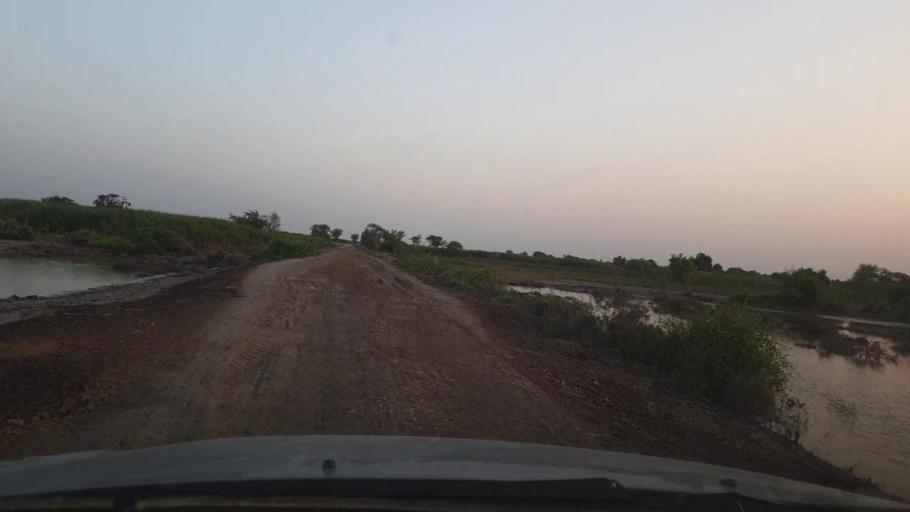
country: PK
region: Sindh
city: Digri
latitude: 25.1166
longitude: 68.9925
